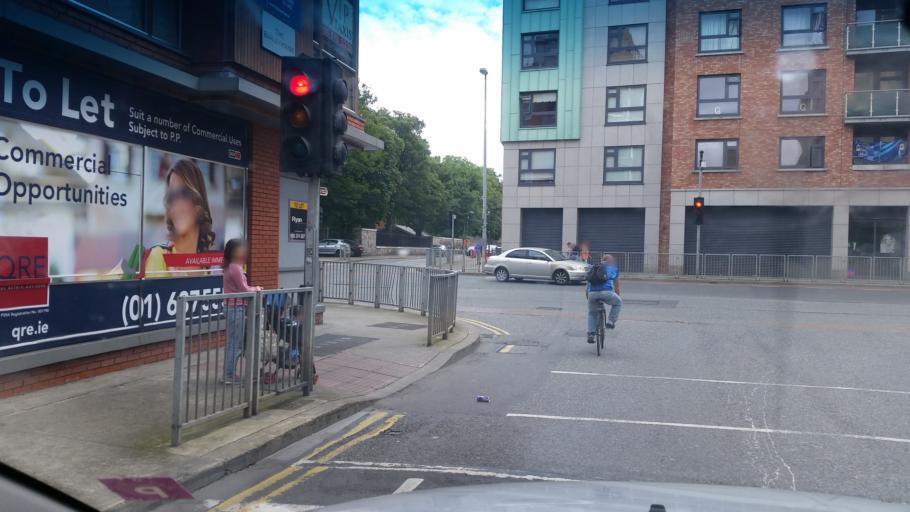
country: IE
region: Leinster
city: Rialto
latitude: 53.3374
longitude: -6.2867
